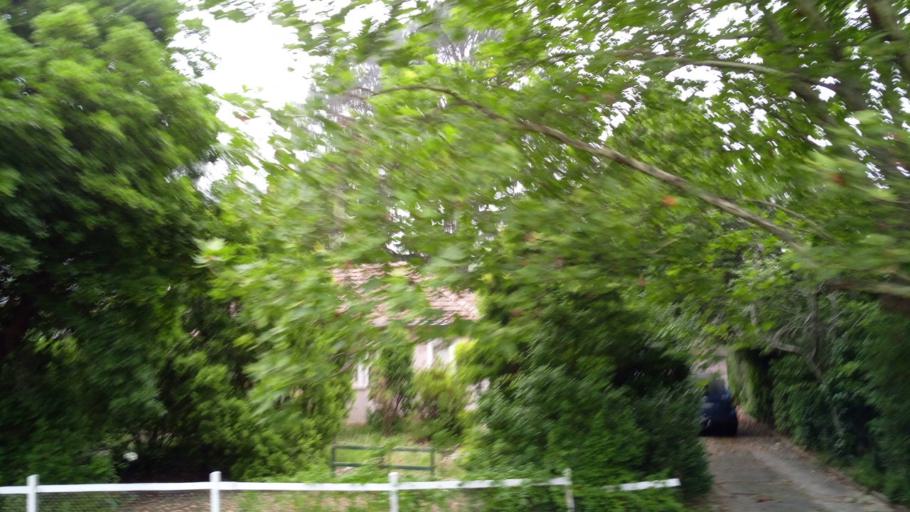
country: AU
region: New South Wales
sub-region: Blue Mountains Municipality
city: Leura
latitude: -33.7185
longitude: 150.3288
